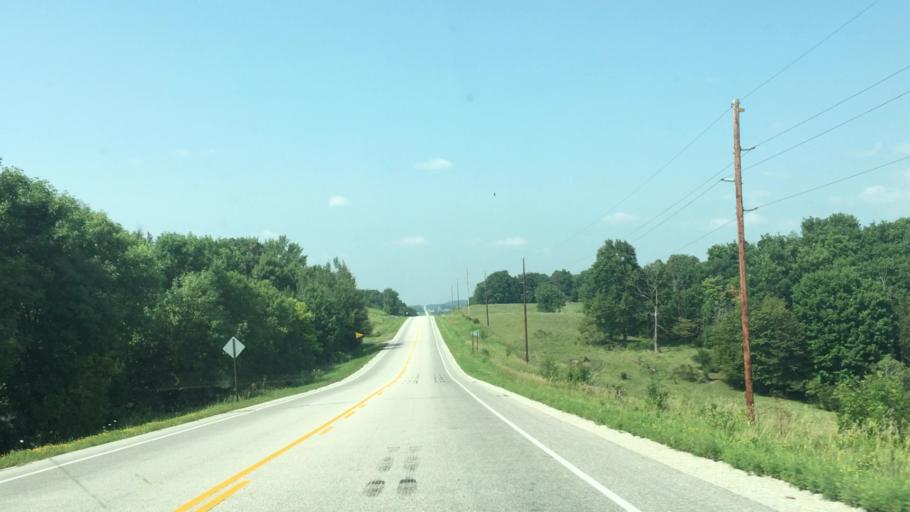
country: US
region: Minnesota
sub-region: Fillmore County
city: Harmony
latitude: 43.5820
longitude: -91.9298
